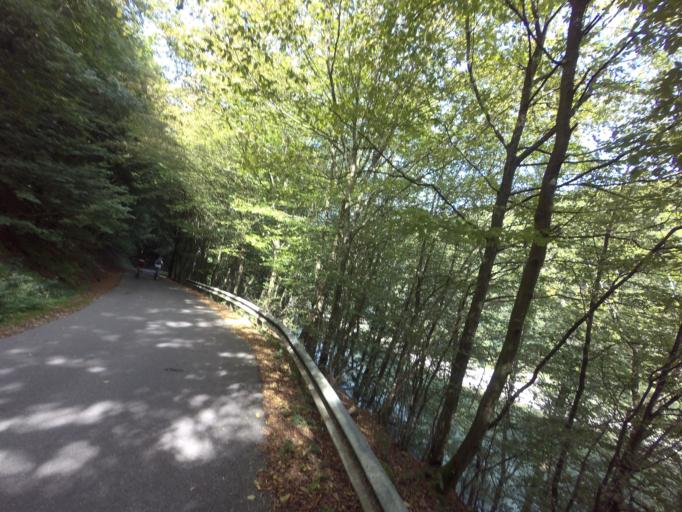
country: DE
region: North Rhine-Westphalia
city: Heimbach
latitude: 50.6360
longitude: 6.3892
